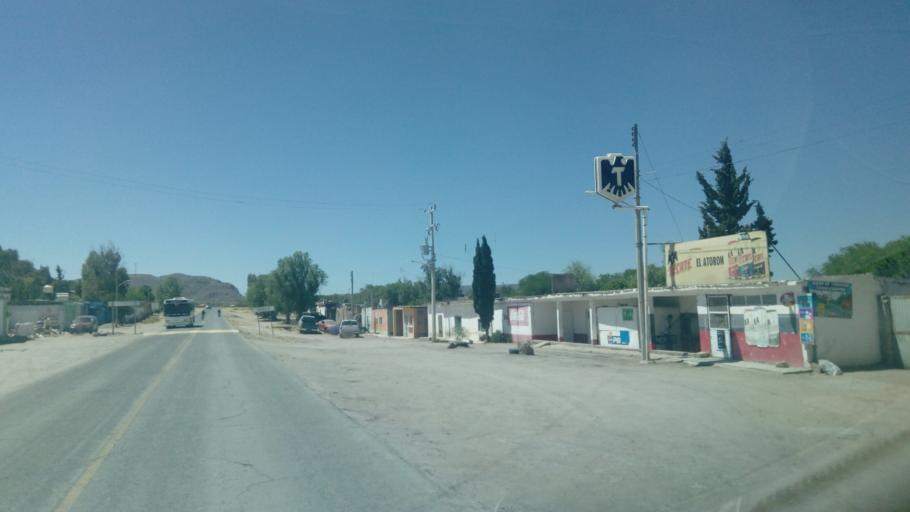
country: MX
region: Durango
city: Victoria de Durango
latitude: 24.1681
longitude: -104.7033
